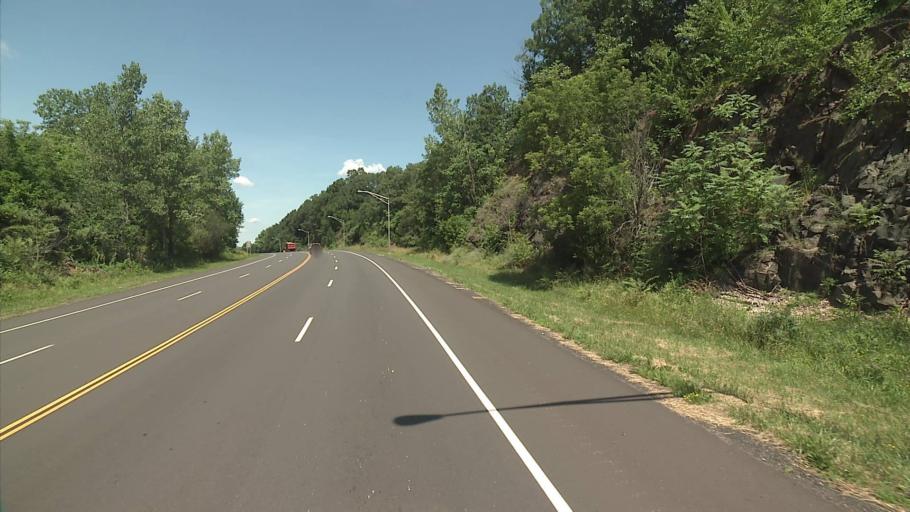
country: US
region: Connecticut
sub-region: Hartford County
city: Kensington
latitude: 41.6233
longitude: -72.7353
